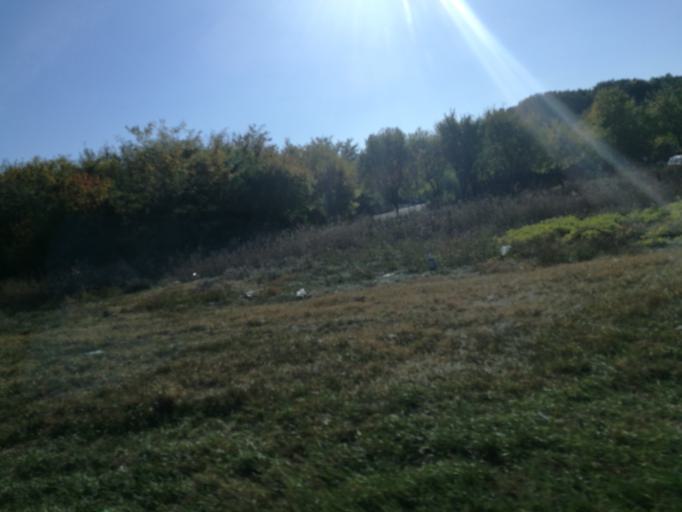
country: RO
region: Ilfov
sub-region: Comuna Dragomiresti-Vale
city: Dragomiresti-Vale
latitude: 44.4712
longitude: 25.9162
